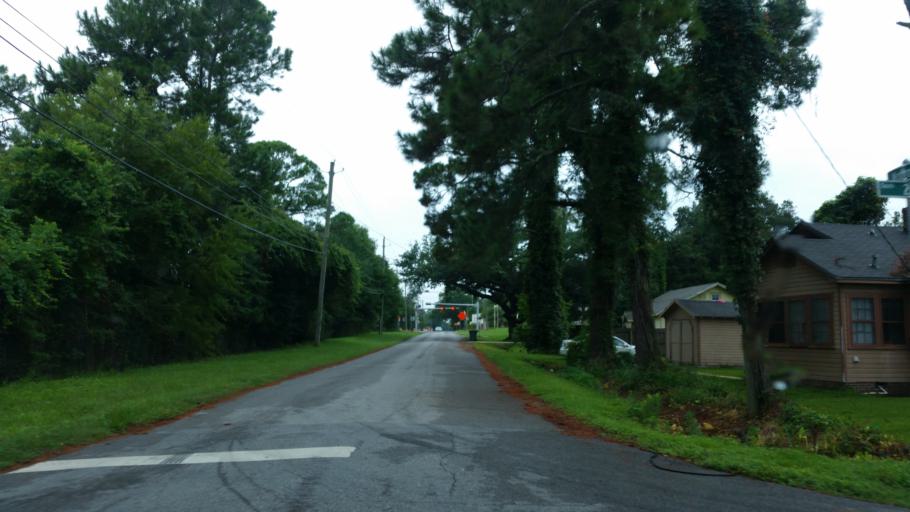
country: US
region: Florida
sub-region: Escambia County
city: Warrington
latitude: 30.3854
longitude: -87.2761
